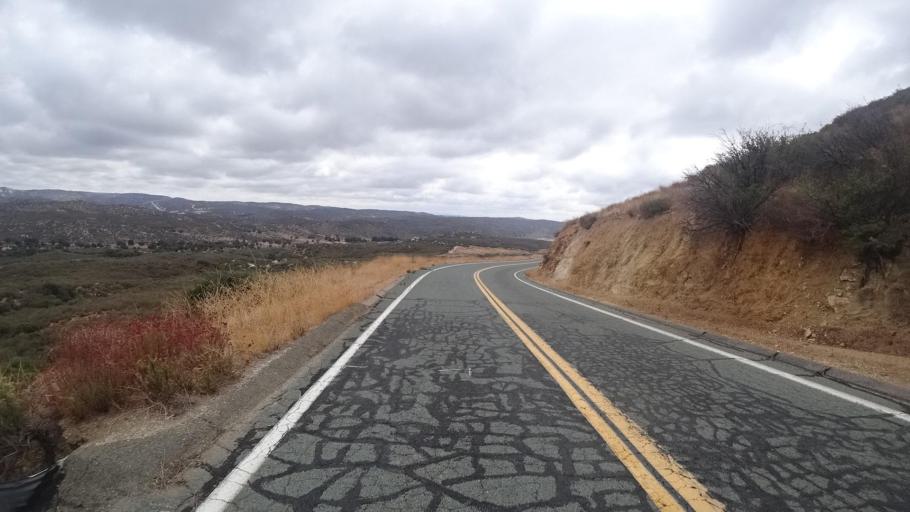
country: US
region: California
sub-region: San Diego County
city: Pine Valley
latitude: 32.7416
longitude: -116.4533
